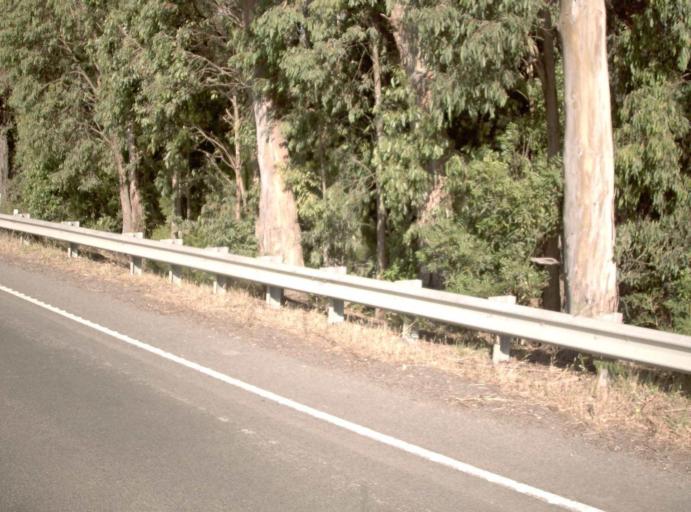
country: AU
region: Victoria
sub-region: Latrobe
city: Morwell
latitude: -38.3793
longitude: 146.2892
